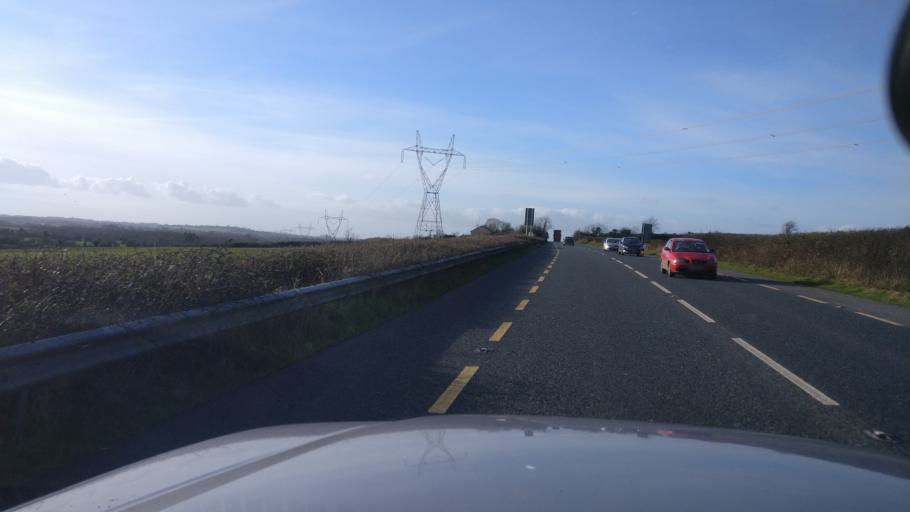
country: IE
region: Leinster
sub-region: Uibh Fhaili
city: Tullamore
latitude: 53.2165
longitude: -7.4593
